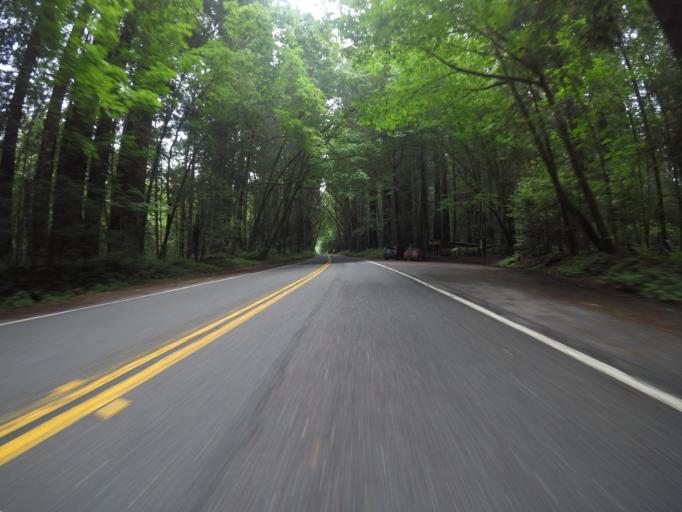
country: US
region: California
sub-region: Humboldt County
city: Rio Dell
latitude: 40.4418
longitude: -124.0311
